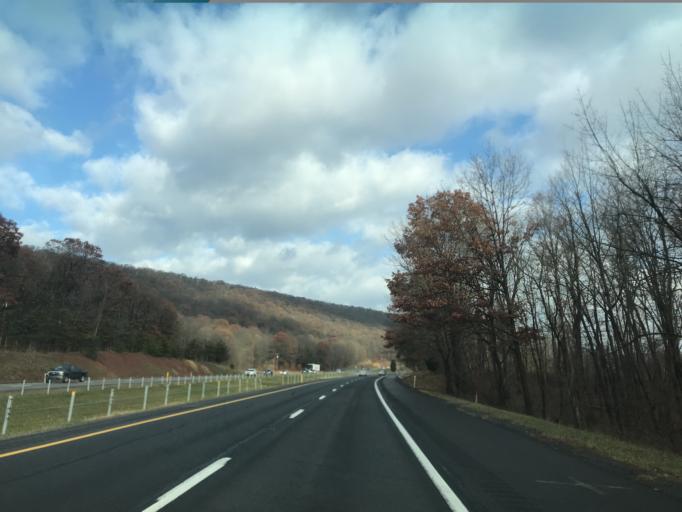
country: US
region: Maryland
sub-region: Washington County
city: Hancock
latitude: 39.8354
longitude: -78.2759
